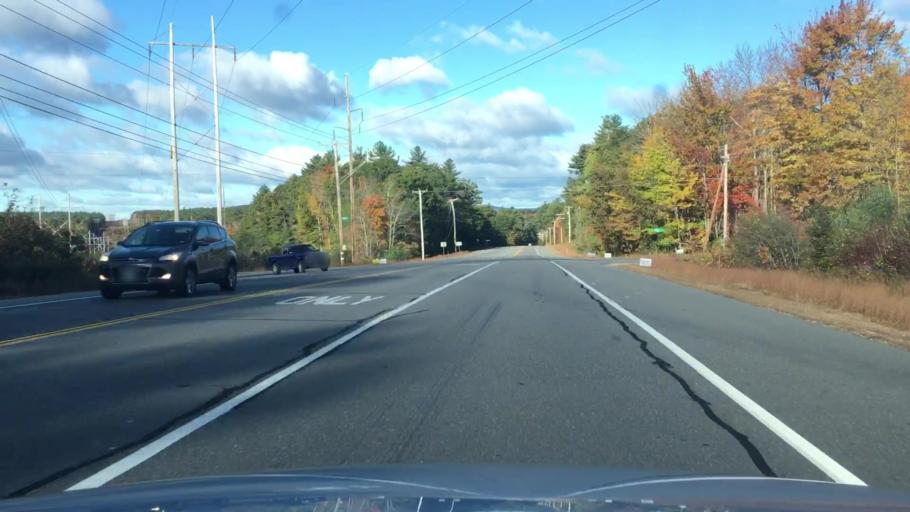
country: US
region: New Hampshire
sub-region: Strafford County
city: Lee
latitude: 43.1544
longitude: -71.0570
